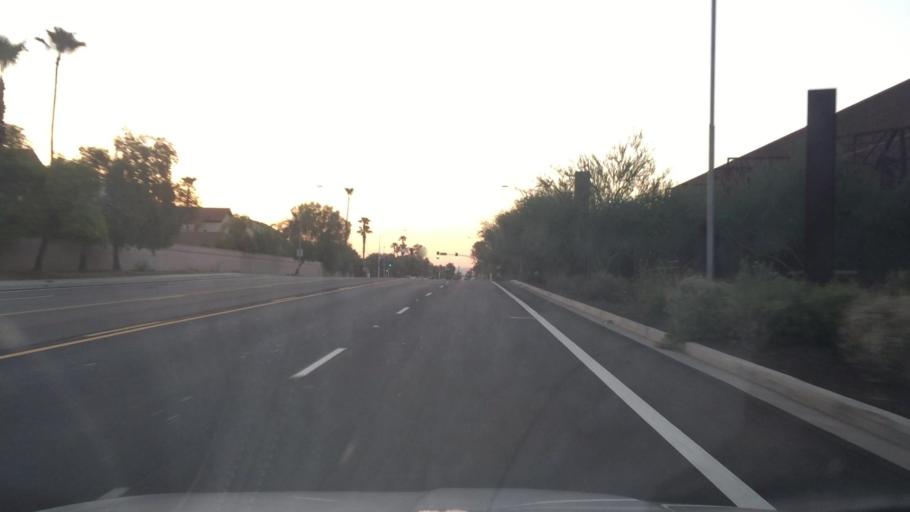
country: US
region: Arizona
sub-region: Maricopa County
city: Scottsdale
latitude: 33.5238
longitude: -111.9066
